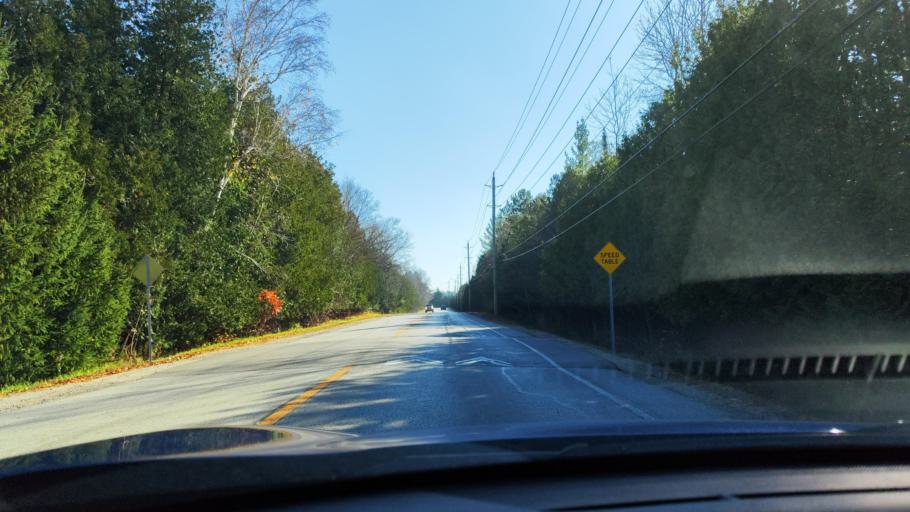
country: CA
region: Ontario
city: Wasaga Beach
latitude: 44.5092
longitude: -79.9962
